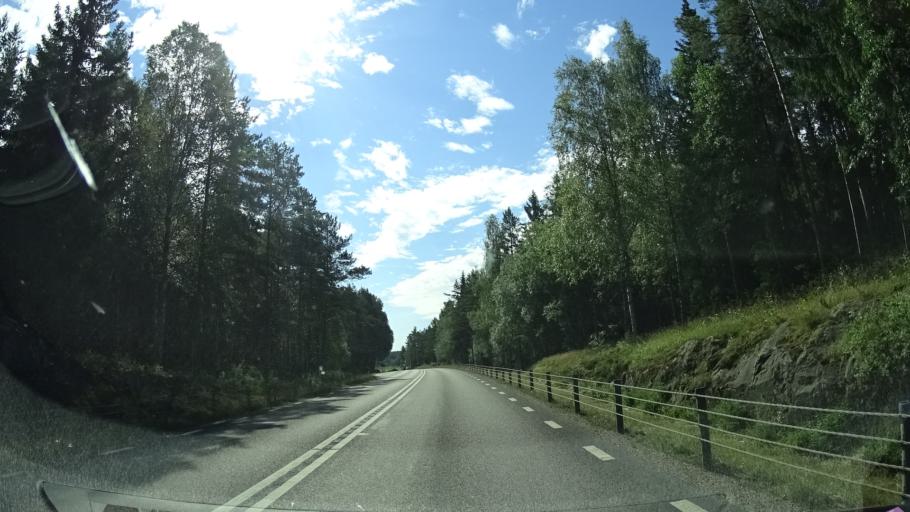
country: SE
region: Vaermland
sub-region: Arjangs Kommun
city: Toecksfors
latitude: 59.4912
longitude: 11.9284
